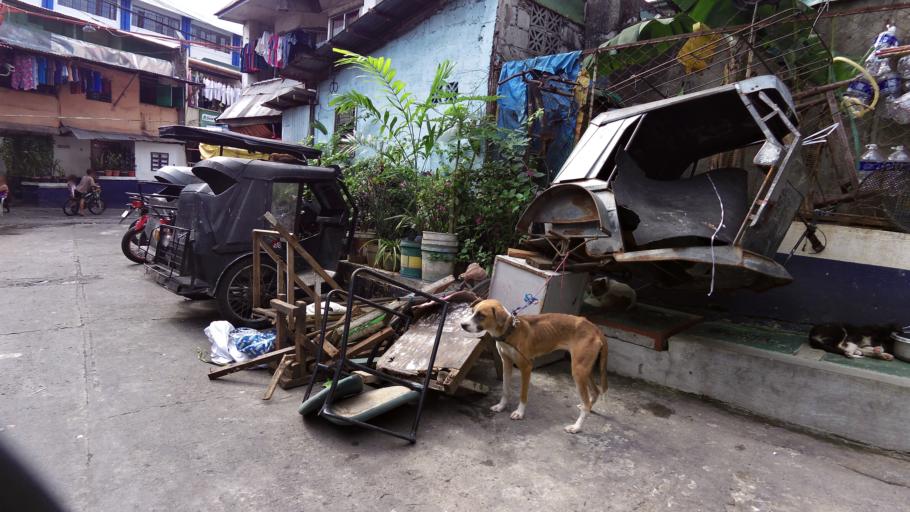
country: PH
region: Metro Manila
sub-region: Pasig
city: Pasig City
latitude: 14.5654
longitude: 121.0611
